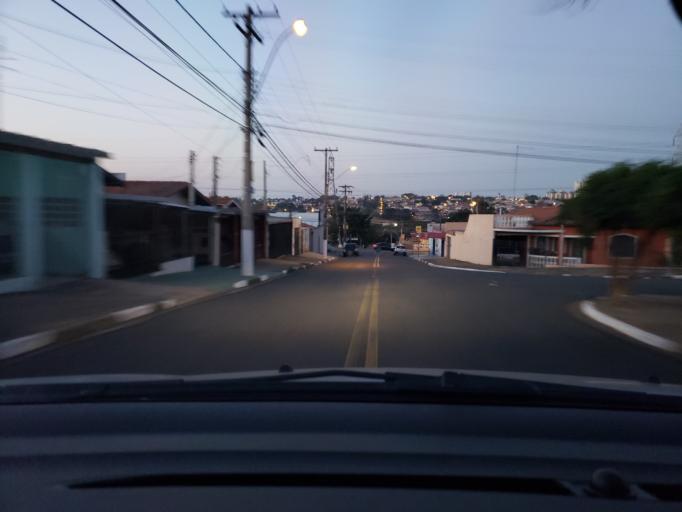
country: BR
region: Sao Paulo
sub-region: Campinas
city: Campinas
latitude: -22.9141
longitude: -47.1056
